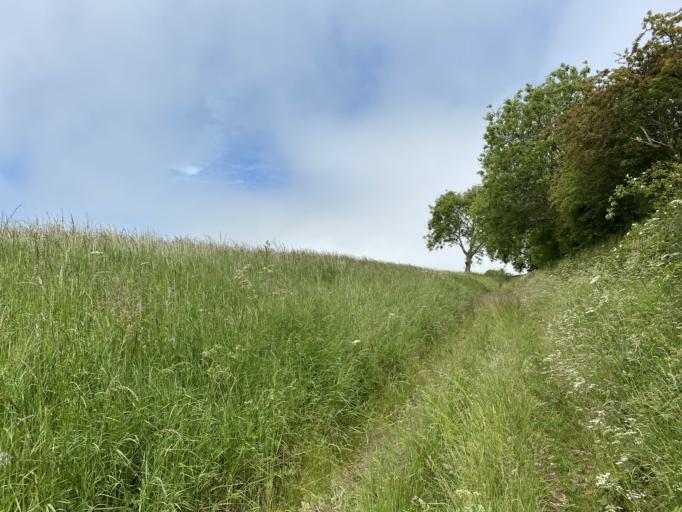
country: GB
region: England
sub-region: East Riding of Yorkshire
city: Wold Newton
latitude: 54.0970
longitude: -0.4749
